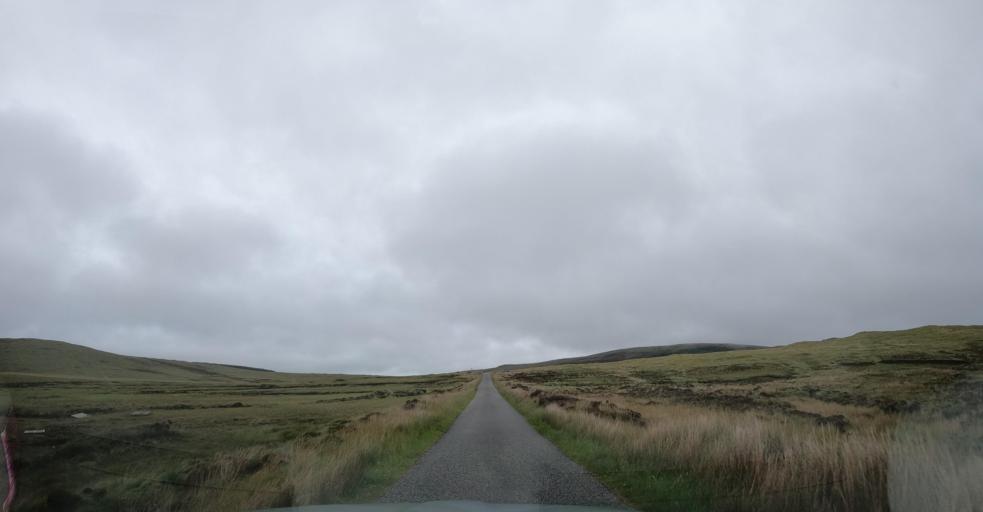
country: GB
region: Scotland
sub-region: Eilean Siar
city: Isle of North Uist
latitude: 57.6019
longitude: -7.3830
